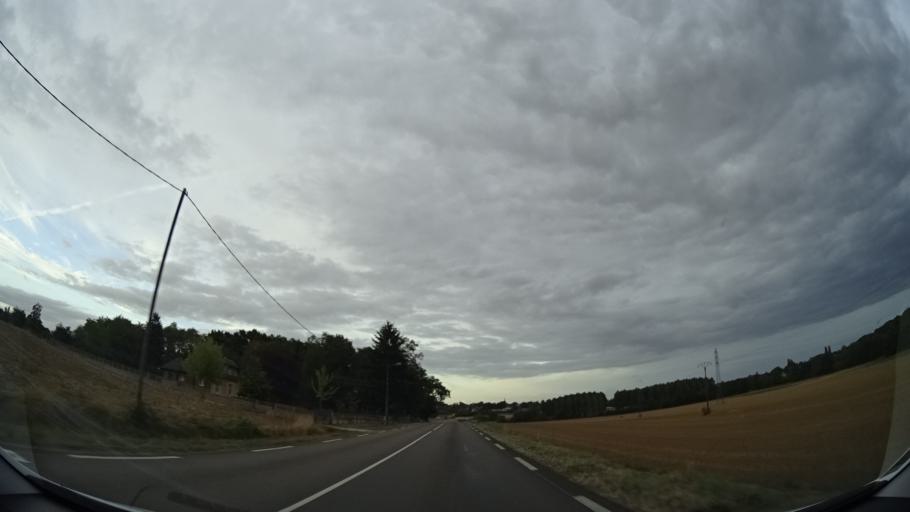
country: FR
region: Bourgogne
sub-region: Departement de l'Yonne
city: Charny
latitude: 47.9365
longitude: 3.1171
